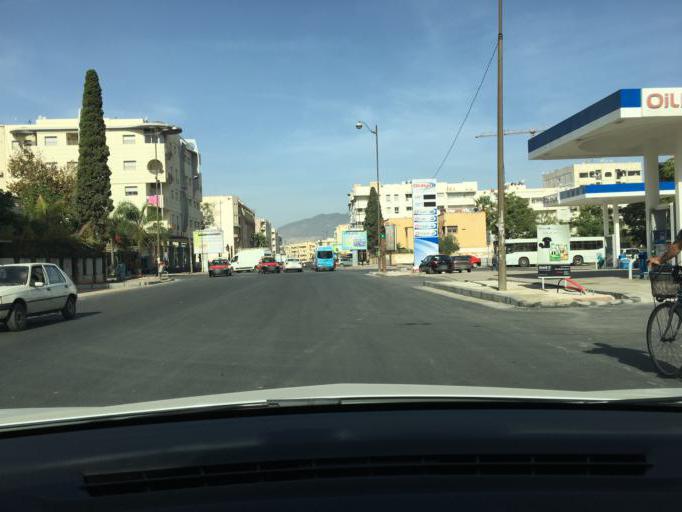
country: MA
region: Fes-Boulemane
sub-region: Fes
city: Fes
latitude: 34.0387
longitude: -5.0062
